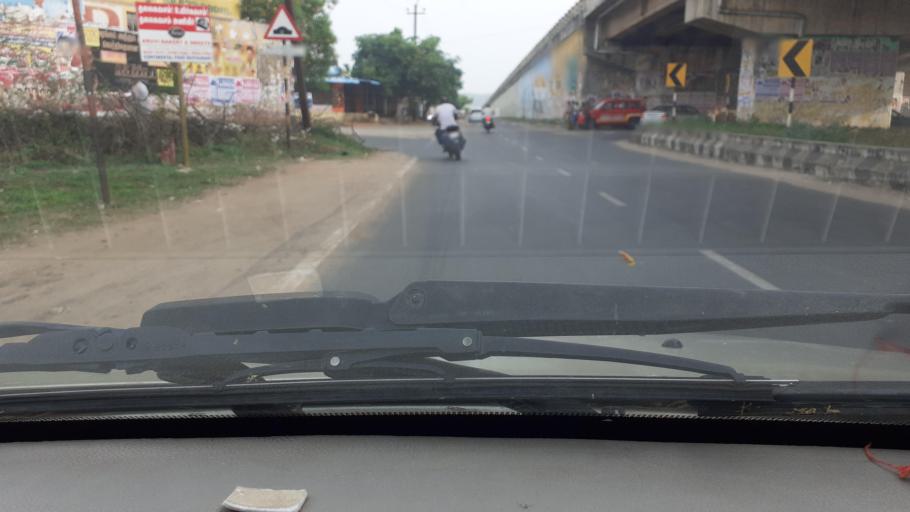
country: IN
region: Tamil Nadu
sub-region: Tirunelveli Kattabo
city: Tirunelveli
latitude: 8.7139
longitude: 77.7655
